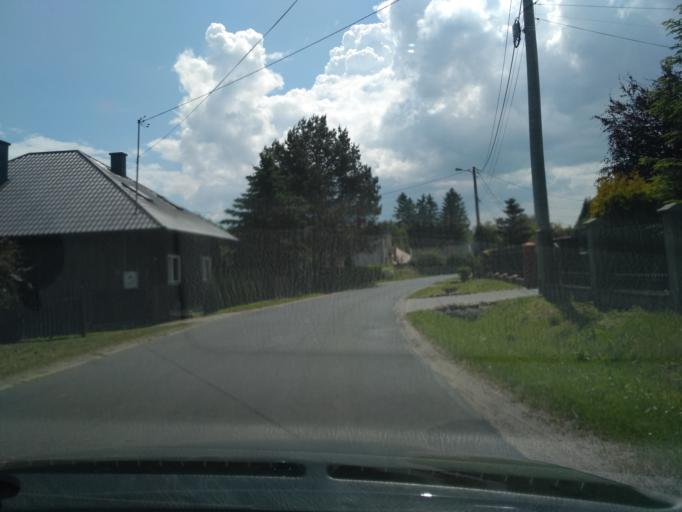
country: PL
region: Subcarpathian Voivodeship
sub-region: Powiat lancucki
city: Sonina
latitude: 50.0590
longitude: 22.2681
